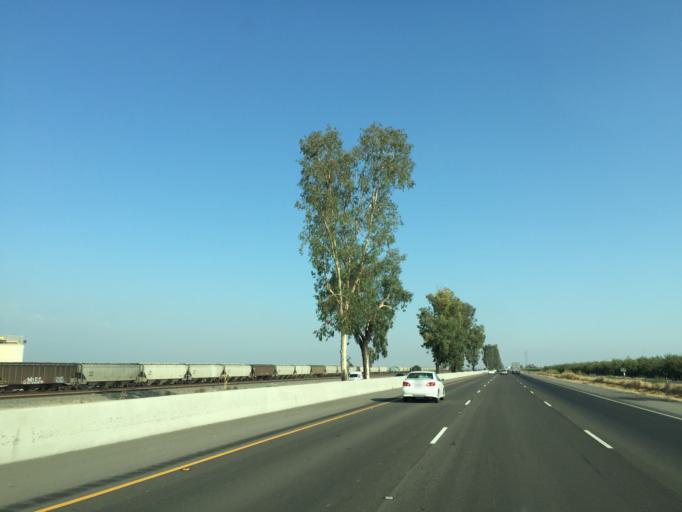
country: US
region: California
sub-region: Tulare County
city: London
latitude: 36.4420
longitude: -119.4814
